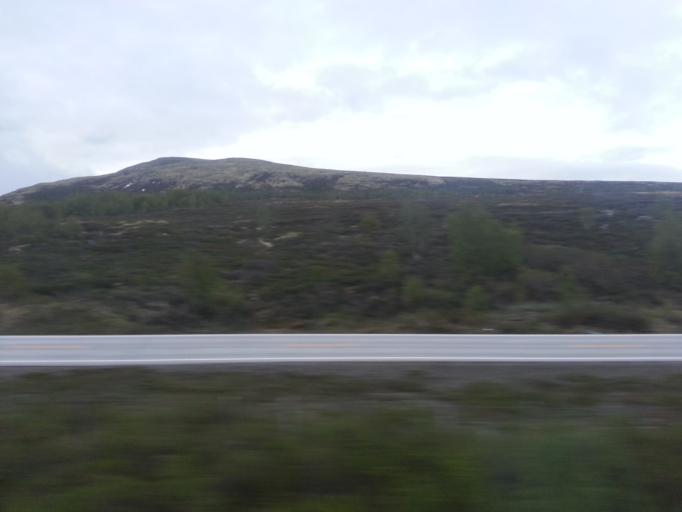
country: NO
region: Sor-Trondelag
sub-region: Oppdal
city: Oppdal
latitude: 62.2489
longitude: 9.5393
